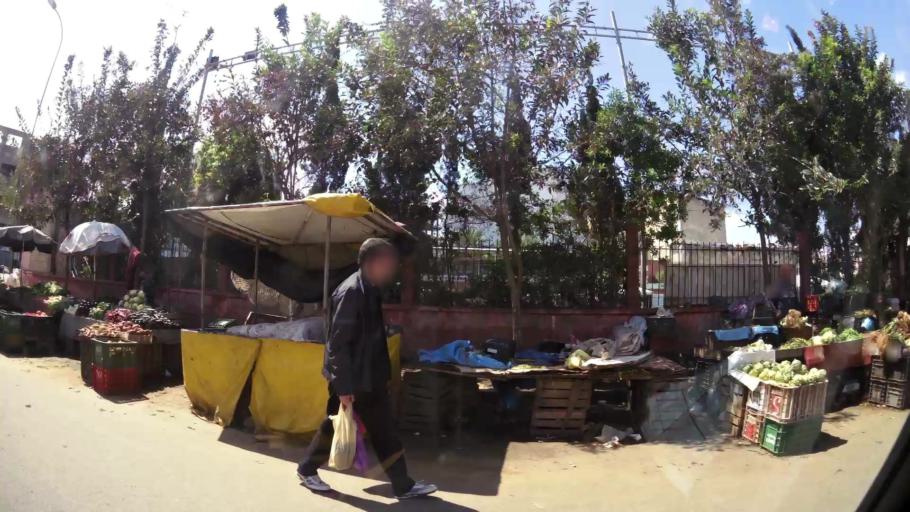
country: MA
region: Grand Casablanca
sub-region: Casablanca
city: Casablanca
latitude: 33.5995
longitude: -7.6276
